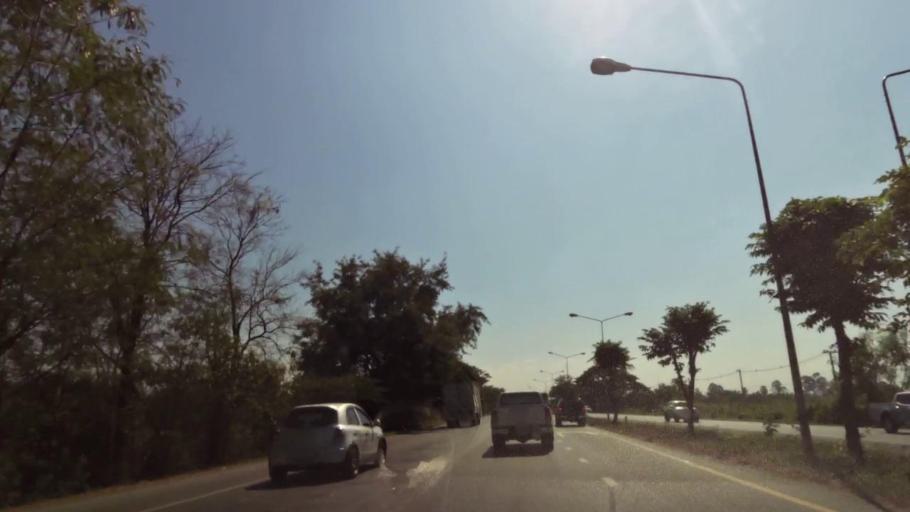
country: TH
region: Nakhon Sawan
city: Kao Liao
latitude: 15.7992
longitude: 100.1204
